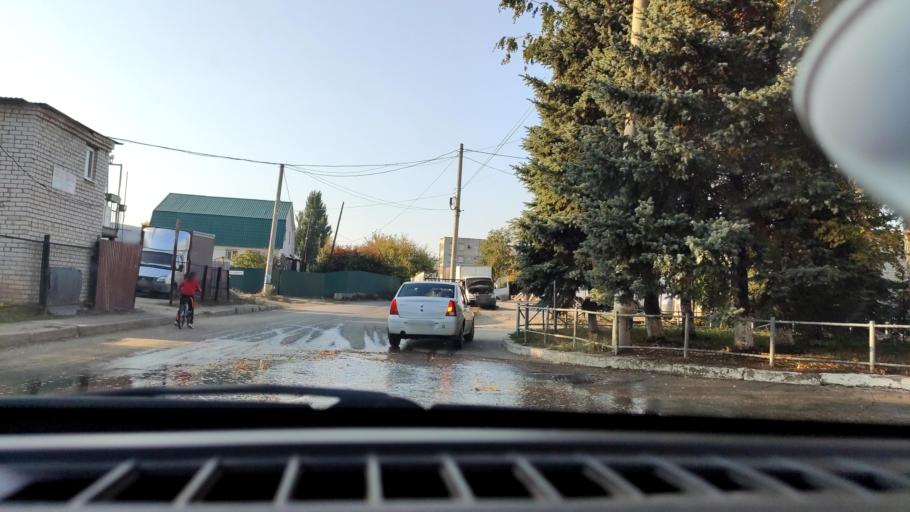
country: RU
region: Samara
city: Samara
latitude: 53.2238
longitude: 50.2274
